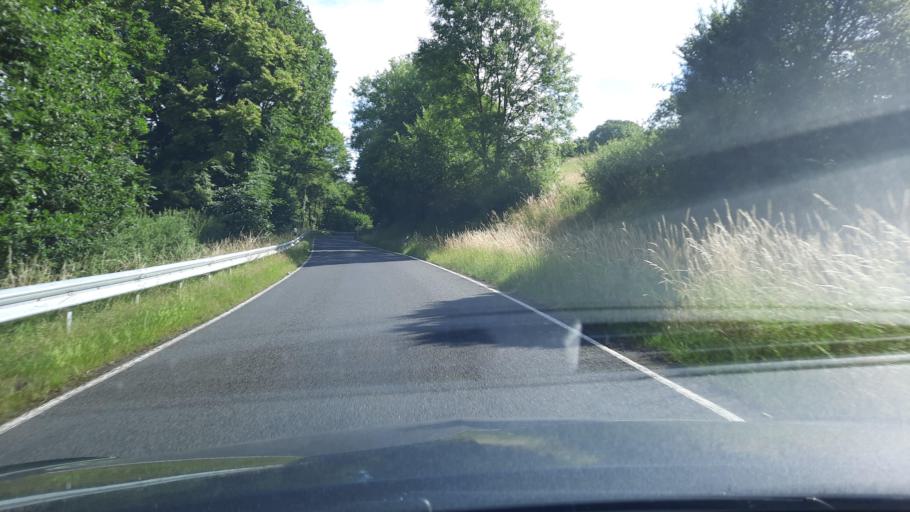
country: DE
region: Rheinland-Pfalz
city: Brenk
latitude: 50.4347
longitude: 7.1766
